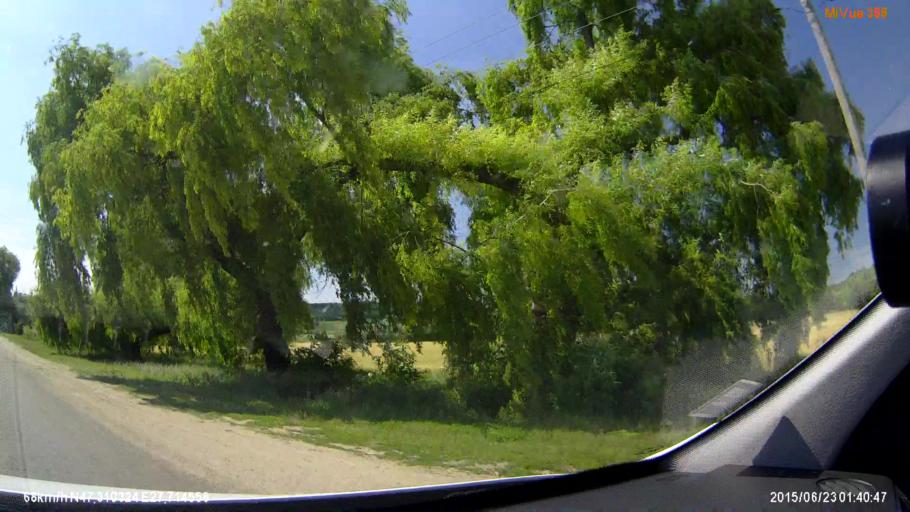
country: RO
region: Iasi
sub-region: Comuna Golaesti
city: Golaesti
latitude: 47.3103
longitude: 27.7148
